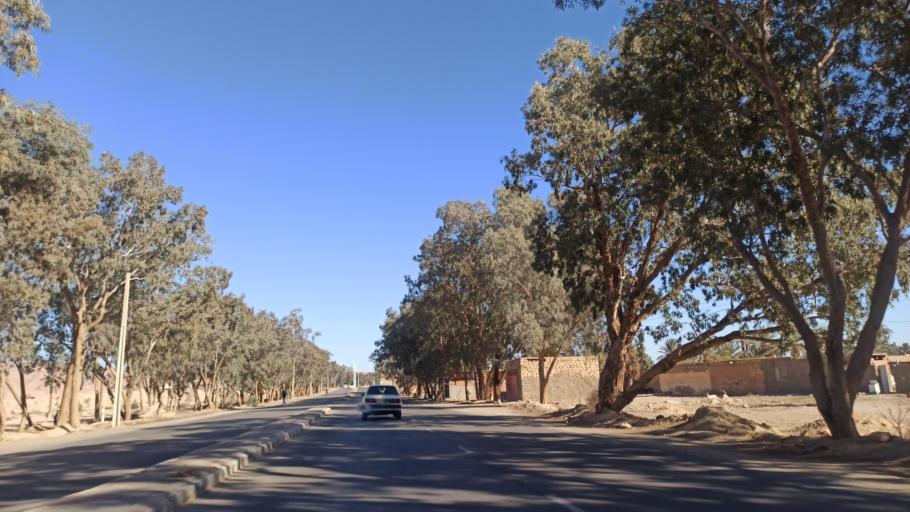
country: TN
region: Gafsa
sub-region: Gafsa Municipality
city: Gafsa
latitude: 34.3982
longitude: 8.7205
